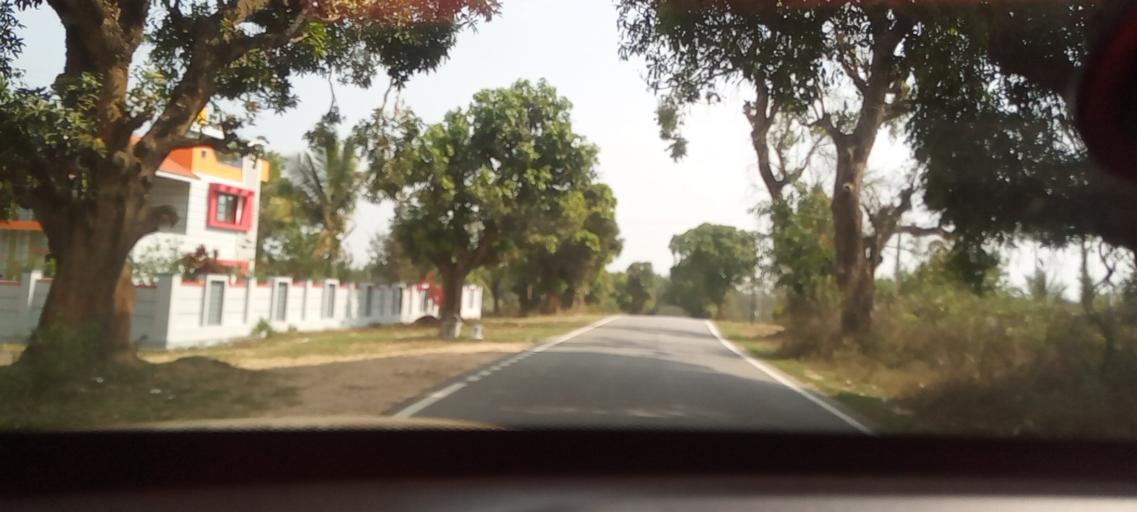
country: IN
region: Karnataka
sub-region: Hassan
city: Belur
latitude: 13.1833
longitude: 75.8019
